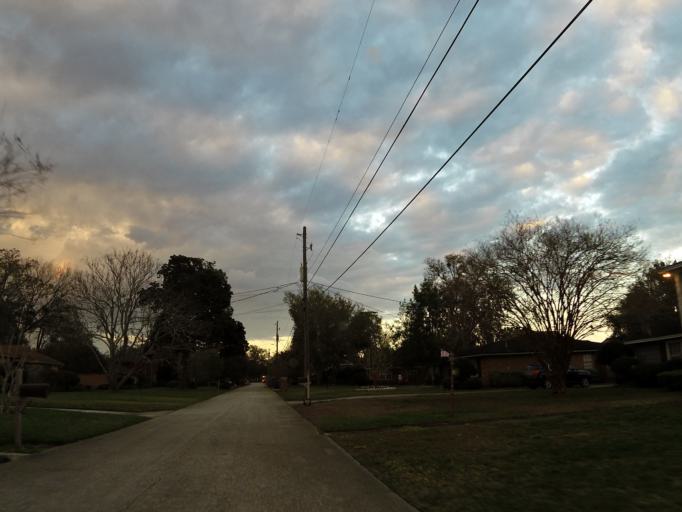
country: US
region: Florida
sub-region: Clay County
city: Orange Park
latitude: 30.2194
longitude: -81.6191
